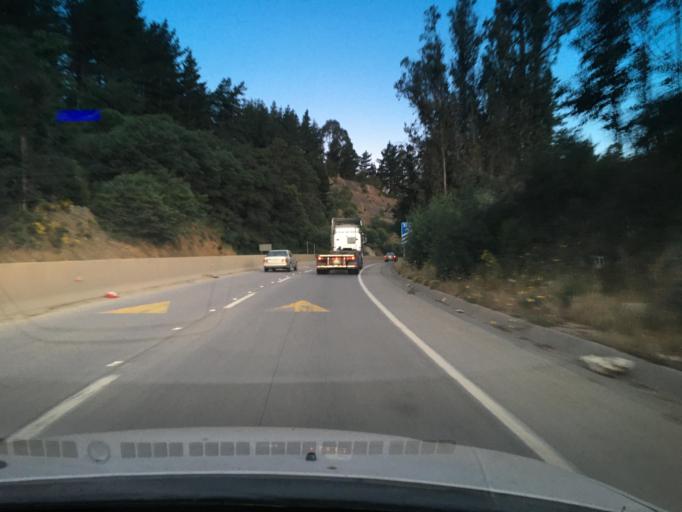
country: CL
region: Valparaiso
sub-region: Provincia de Valparaiso
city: Vina del Mar
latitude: -33.1058
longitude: -71.5597
